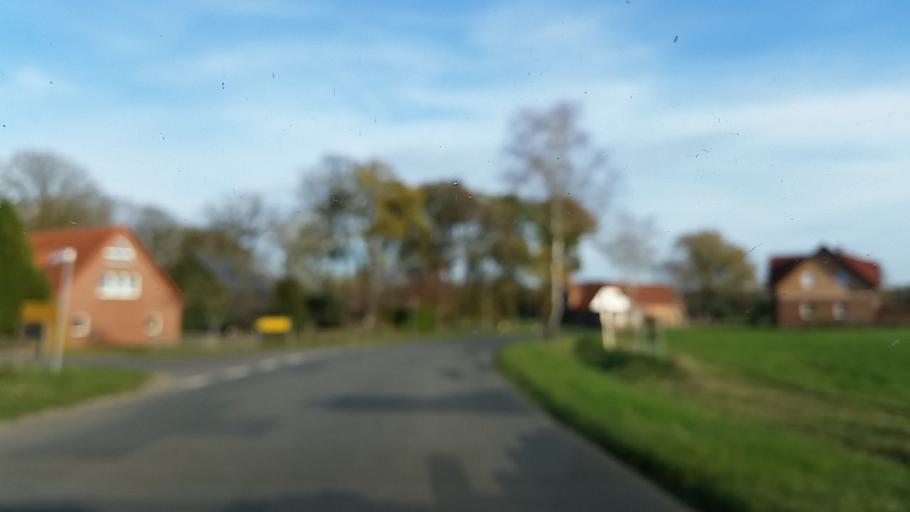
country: DE
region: Lower Saxony
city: Dedelstorf
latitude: 52.6769
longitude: 10.5230
